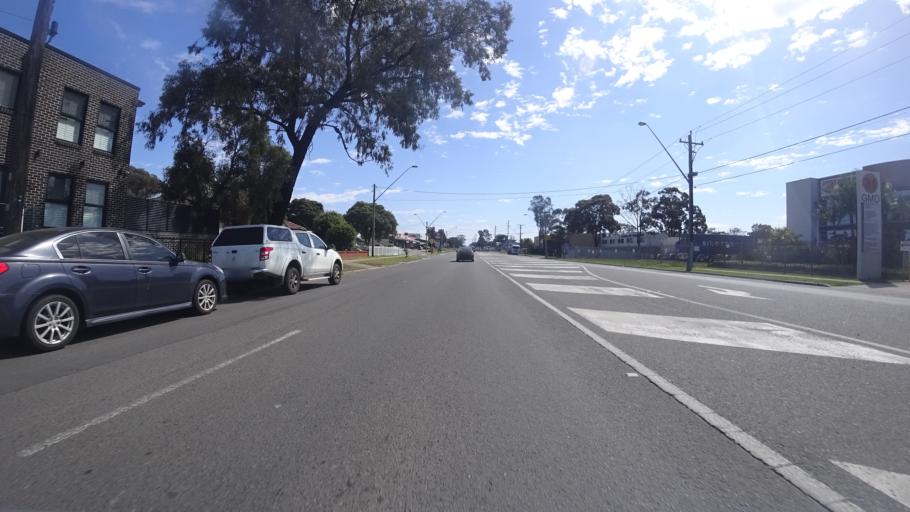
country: AU
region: New South Wales
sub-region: Bankstown
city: Milperra
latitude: -33.9249
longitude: 150.9621
